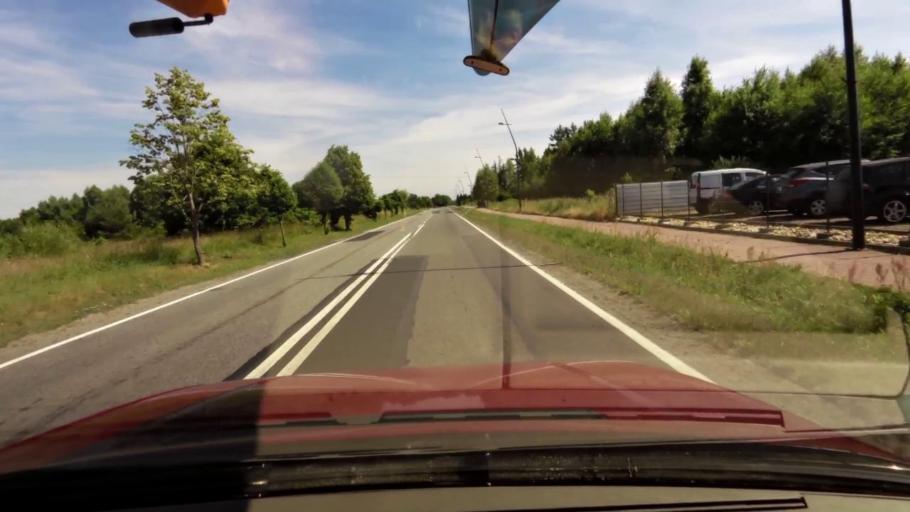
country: PL
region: Pomeranian Voivodeship
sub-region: Powiat slupski
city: Kobylnica
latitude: 54.4325
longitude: 17.0021
